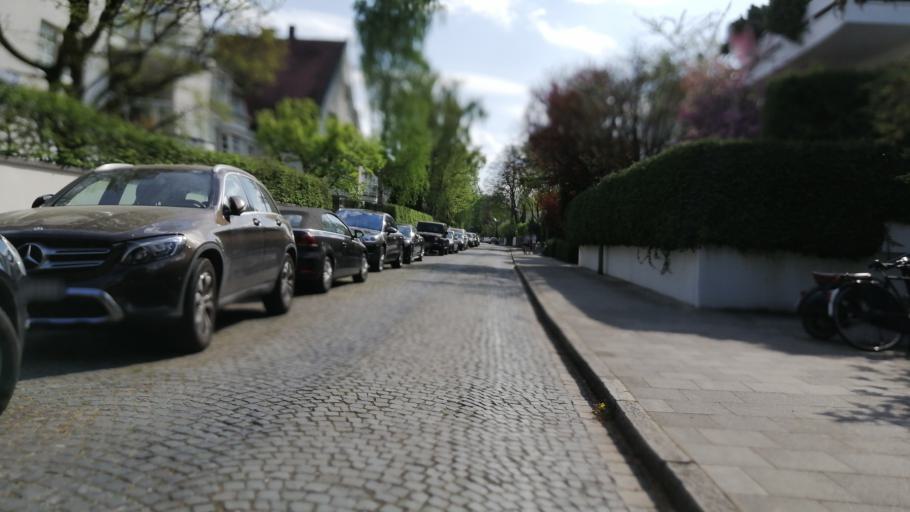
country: DE
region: Bavaria
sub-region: Upper Bavaria
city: Bogenhausen
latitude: 48.1595
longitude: 11.6138
